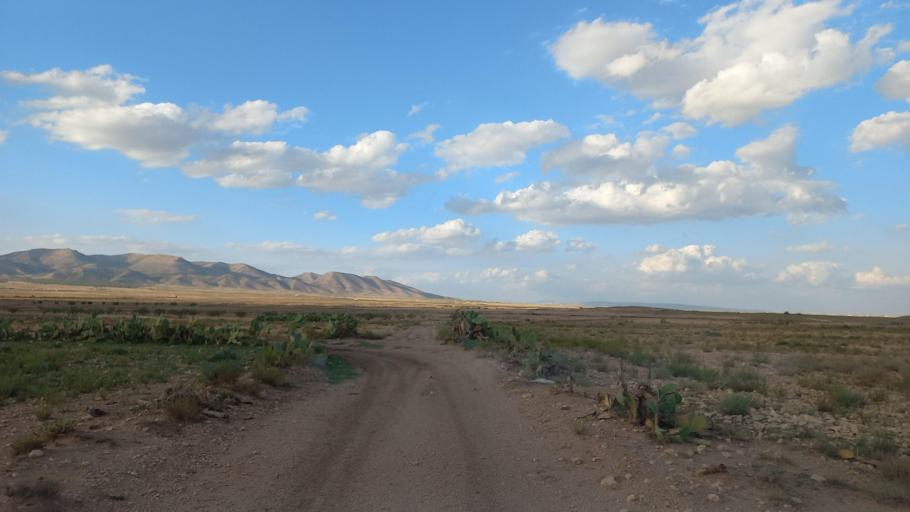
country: TN
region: Al Qasrayn
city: Sbiba
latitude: 35.3915
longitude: 9.0457
